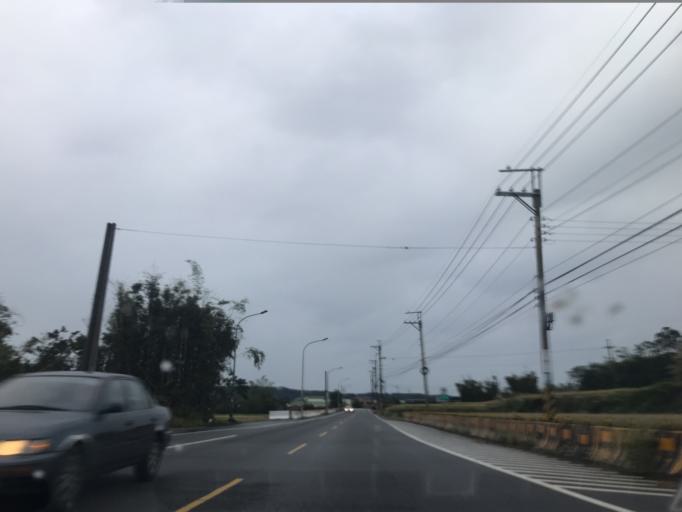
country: TW
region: Taiwan
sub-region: Hsinchu
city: Zhubei
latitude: 24.8336
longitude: 121.0923
